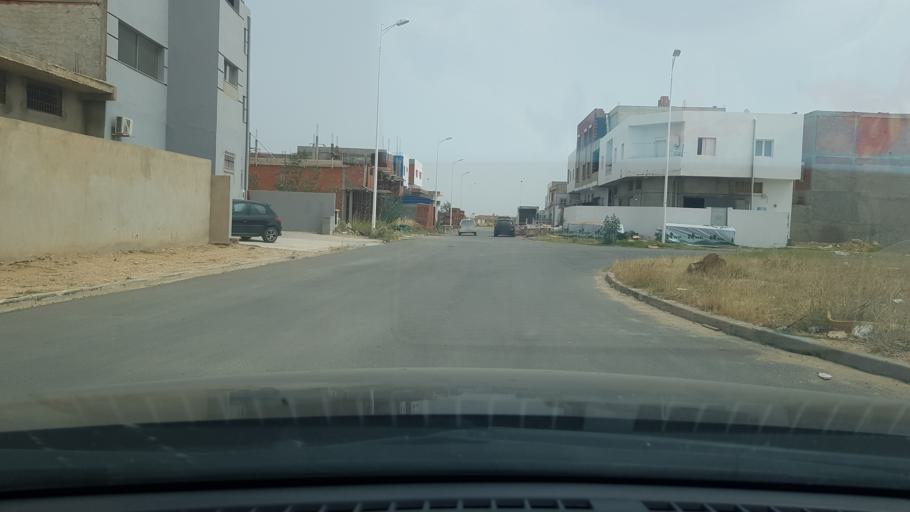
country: TN
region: Safaqis
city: Al Qarmadah
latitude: 34.8262
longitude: 10.7401
